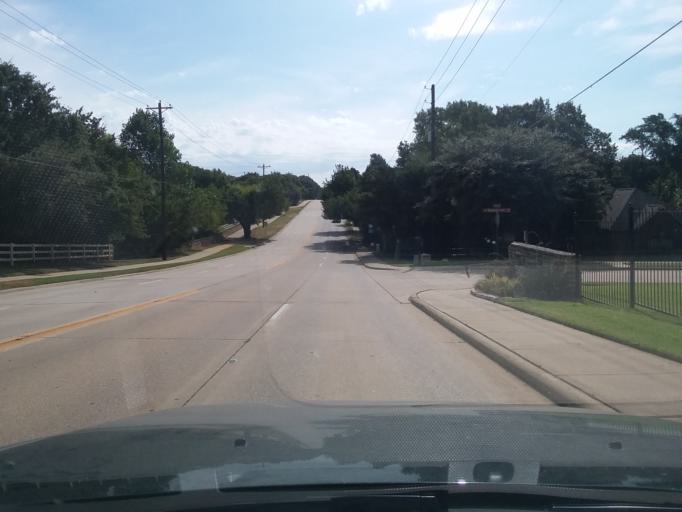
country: US
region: Texas
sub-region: Denton County
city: Flower Mound
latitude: 33.0137
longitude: -97.0827
